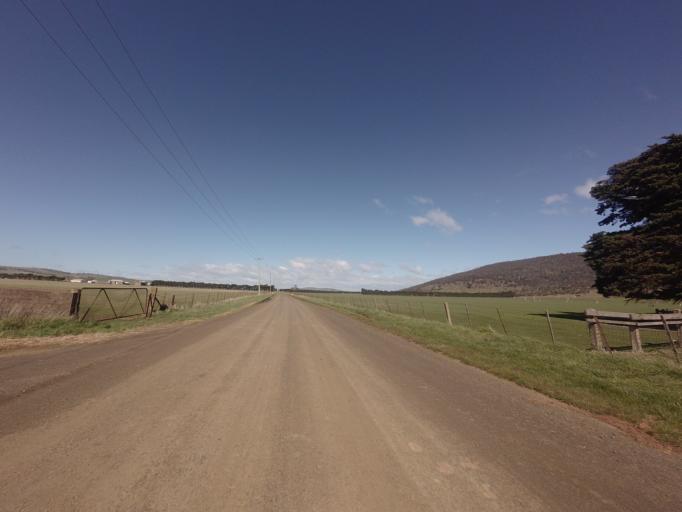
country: AU
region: Tasmania
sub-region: Northern Midlands
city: Evandale
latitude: -41.9572
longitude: 147.4368
